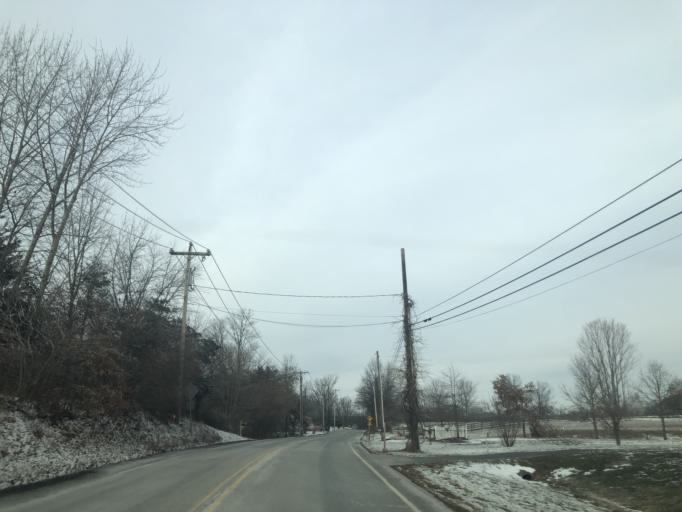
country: US
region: New Jersey
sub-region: Warren County
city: Belvidere
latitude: 40.9375
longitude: -75.0172
